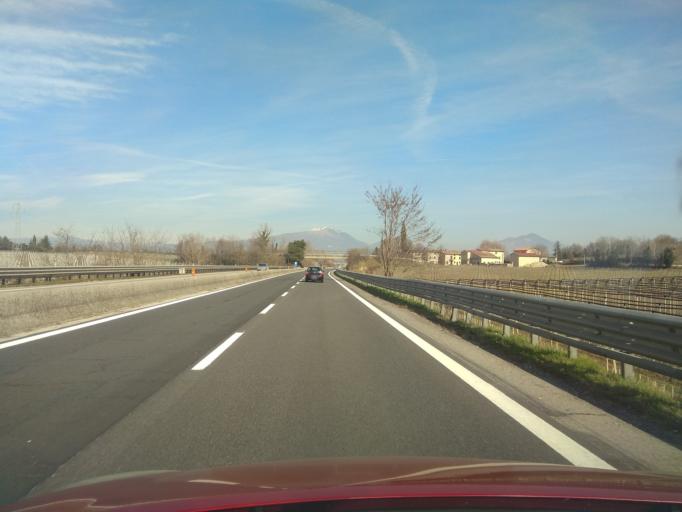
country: IT
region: Veneto
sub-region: Provincia di Verona
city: Cola
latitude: 45.4698
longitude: 10.7612
